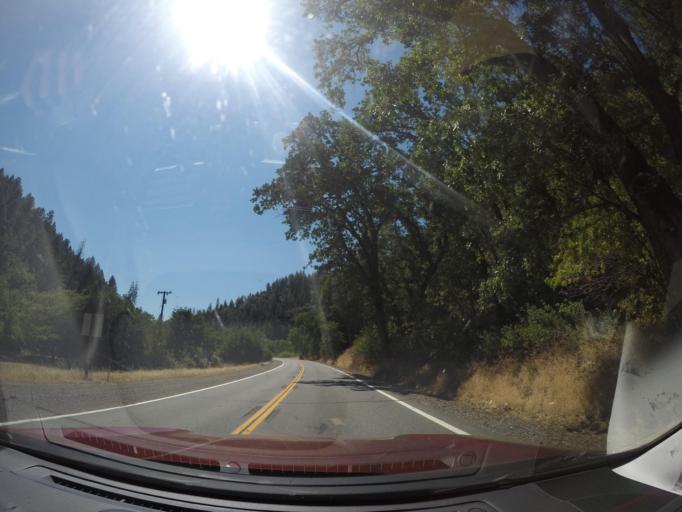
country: US
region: California
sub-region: Shasta County
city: Bella Vista
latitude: 40.7516
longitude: -122.0429
